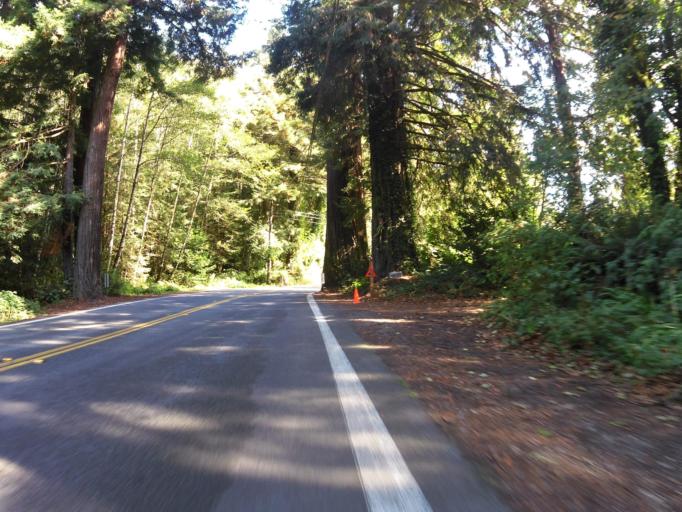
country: US
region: California
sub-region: Del Norte County
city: Bertsch-Oceanview
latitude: 41.8444
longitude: -124.1150
